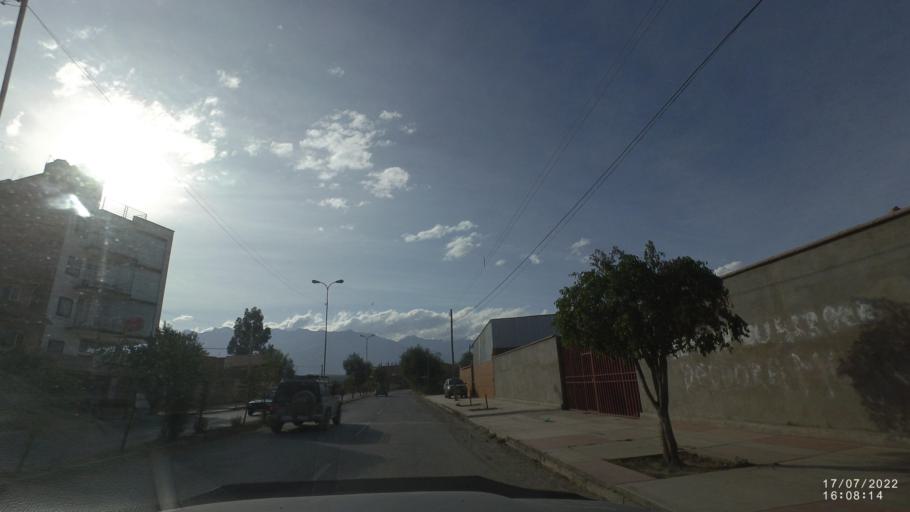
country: BO
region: Cochabamba
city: Sipe Sipe
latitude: -17.4107
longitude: -66.2727
